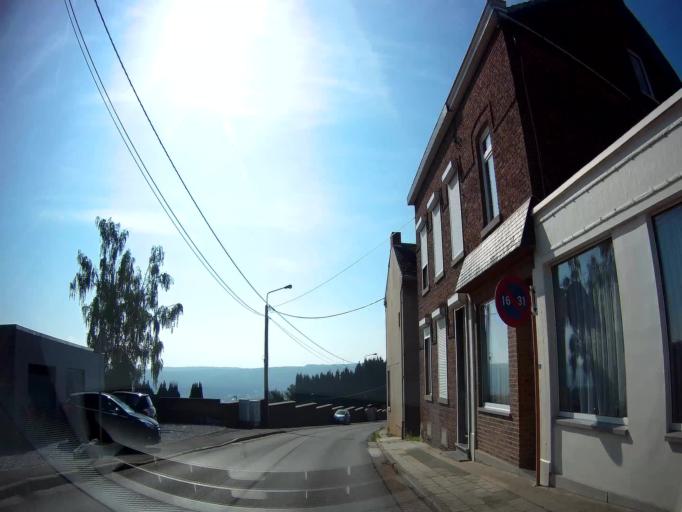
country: BE
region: Wallonia
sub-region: Province de Liege
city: Amay
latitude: 50.5513
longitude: 5.3097
